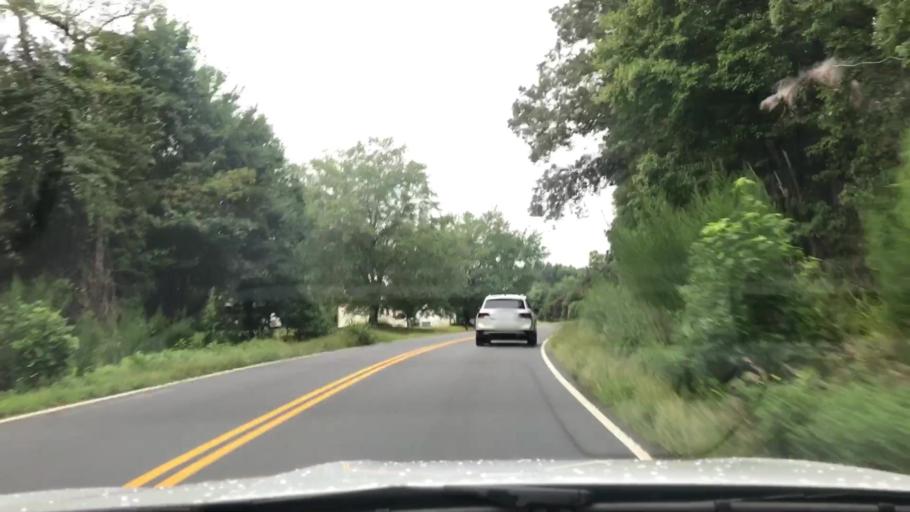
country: US
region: South Carolina
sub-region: Spartanburg County
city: Roebuck
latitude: 34.8259
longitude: -81.9544
